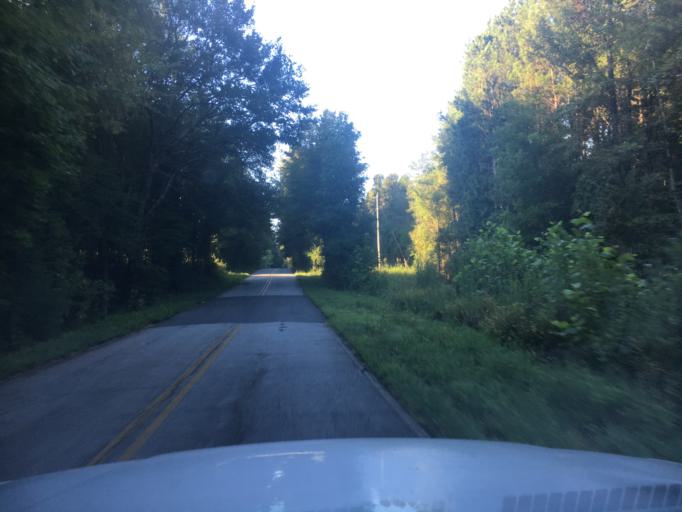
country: US
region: South Carolina
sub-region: Spartanburg County
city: Woodruff
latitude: 34.6785
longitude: -81.9616
